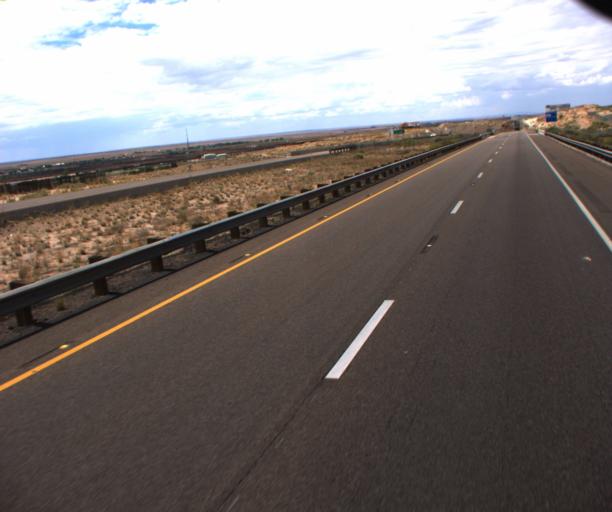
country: US
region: Arizona
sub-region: Navajo County
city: Holbrook
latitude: 34.9112
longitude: -110.1676
